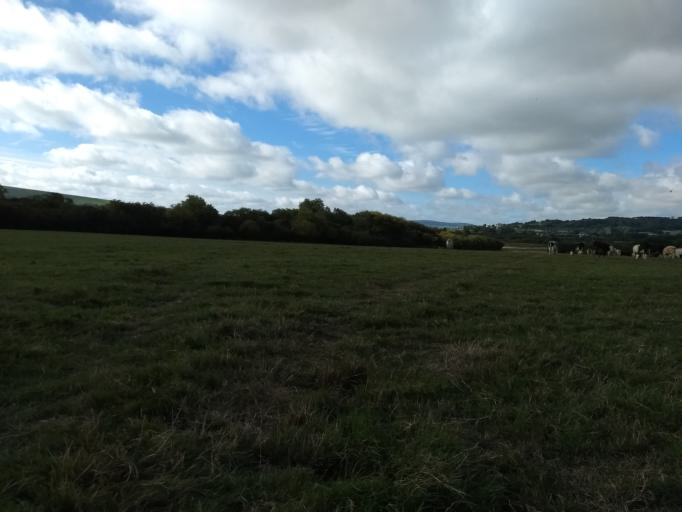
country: GB
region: England
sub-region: Isle of Wight
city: Brading
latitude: 50.6922
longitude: -1.1246
